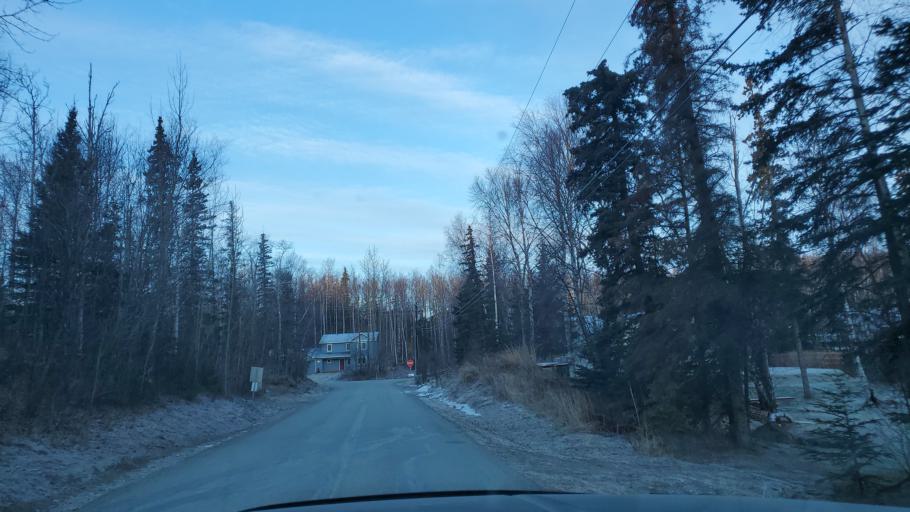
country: US
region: Alaska
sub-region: Matanuska-Susitna Borough
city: Lakes
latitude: 61.6034
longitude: -149.3182
